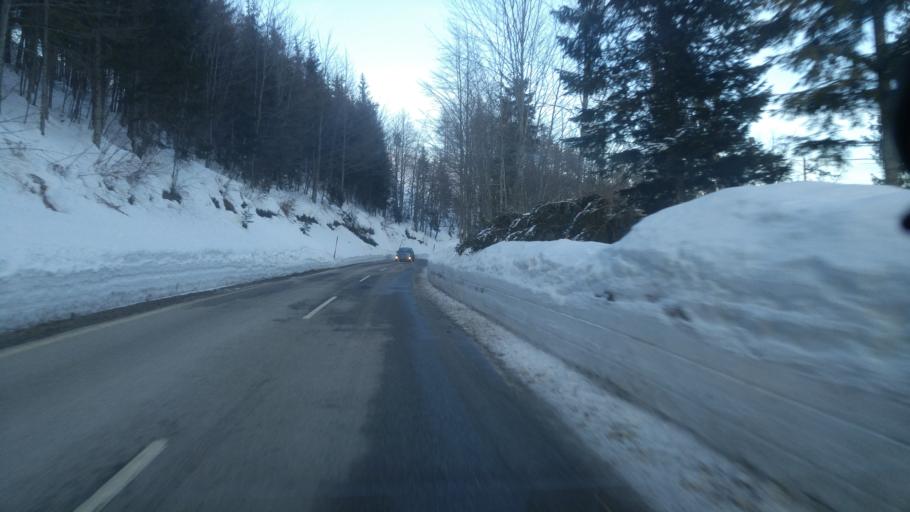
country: AT
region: Lower Austria
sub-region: Politischer Bezirk Lilienfeld
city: Hohenberg
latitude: 47.8862
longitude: 15.6526
